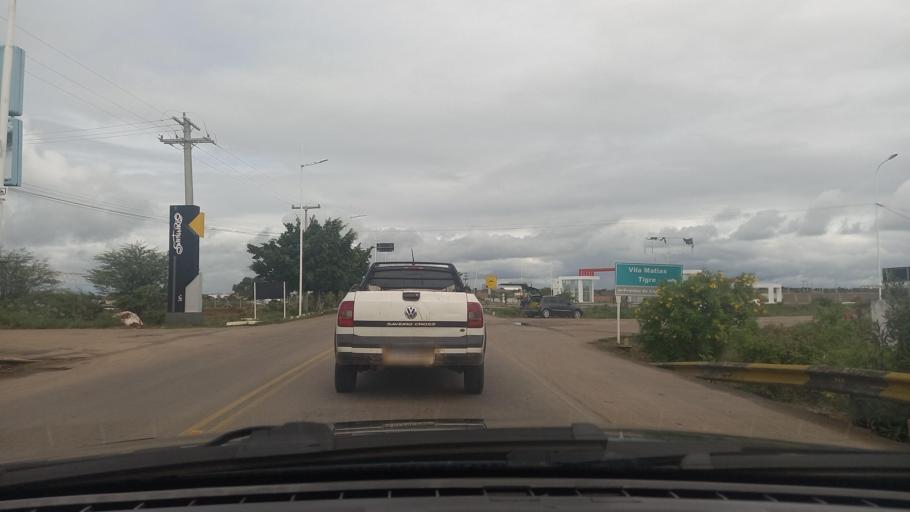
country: BR
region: Bahia
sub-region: Paulo Afonso
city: Paulo Afonso
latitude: -9.4318
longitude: -38.2274
